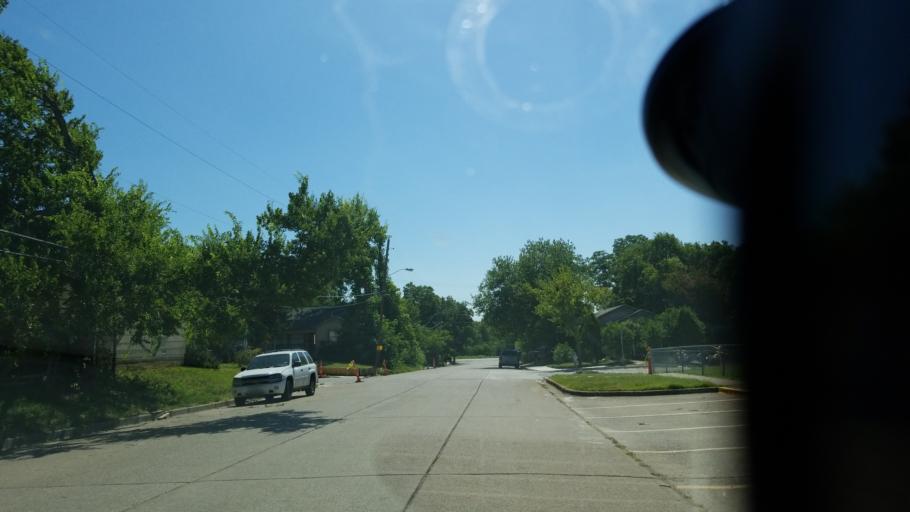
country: US
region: Texas
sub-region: Dallas County
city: Dallas
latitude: 32.7095
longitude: -96.8113
